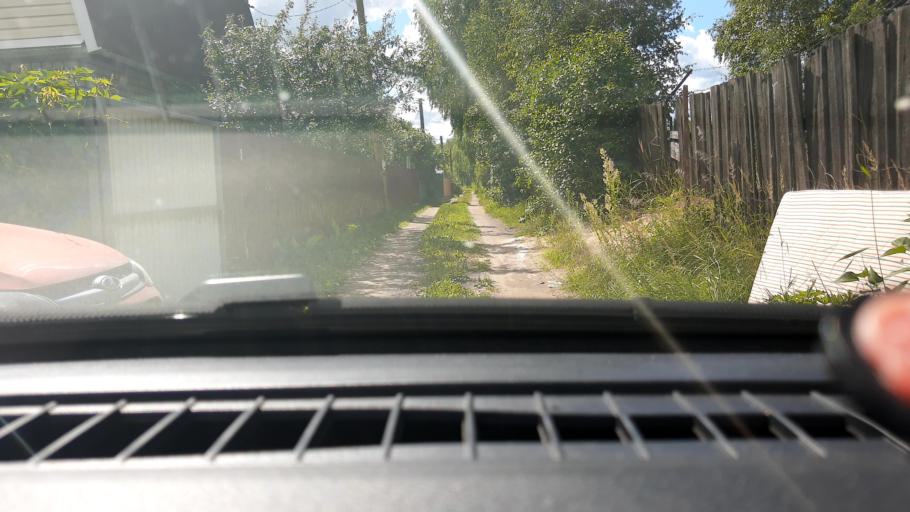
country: RU
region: Nizjnij Novgorod
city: Gorbatovka
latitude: 56.3219
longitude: 43.8264
